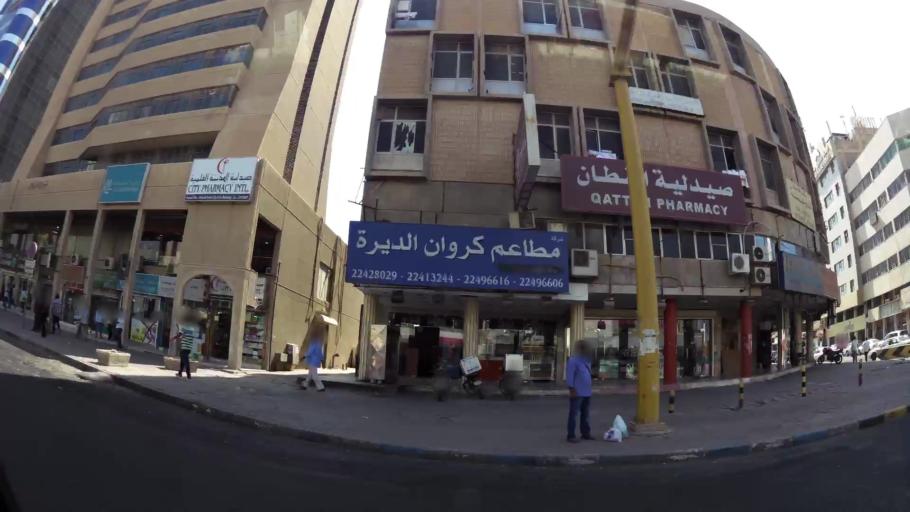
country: KW
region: Al Asimah
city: Kuwait City
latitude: 29.3686
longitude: 47.9776
